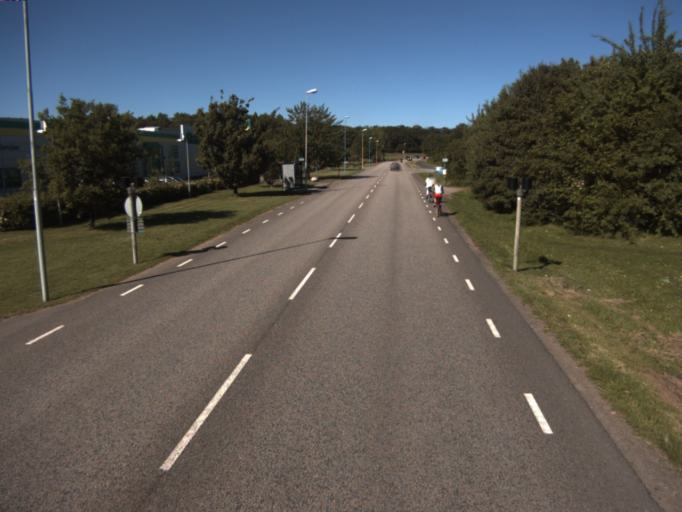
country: SE
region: Skane
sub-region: Helsingborg
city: Odakra
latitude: 56.0827
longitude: 12.7337
